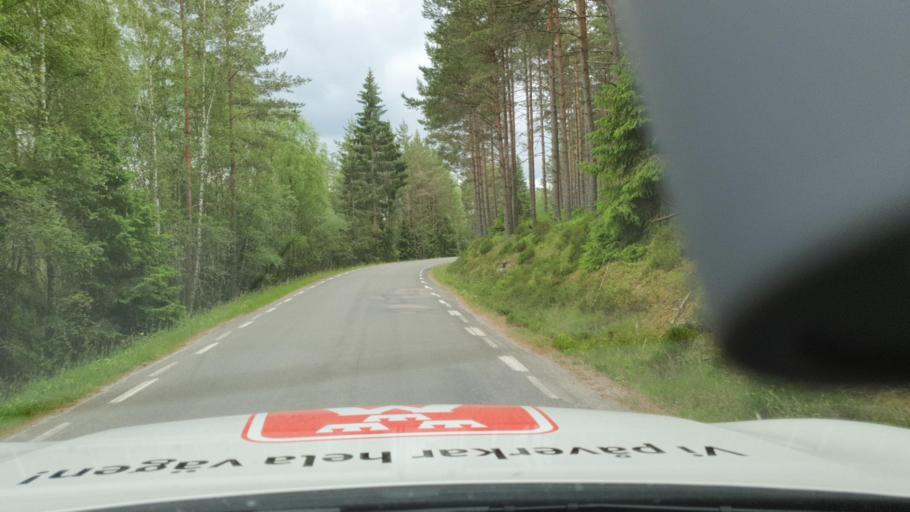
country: SE
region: Vaestra Goetaland
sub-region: Tidaholms Kommun
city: Olofstorp
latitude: 58.1908
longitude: 14.1292
